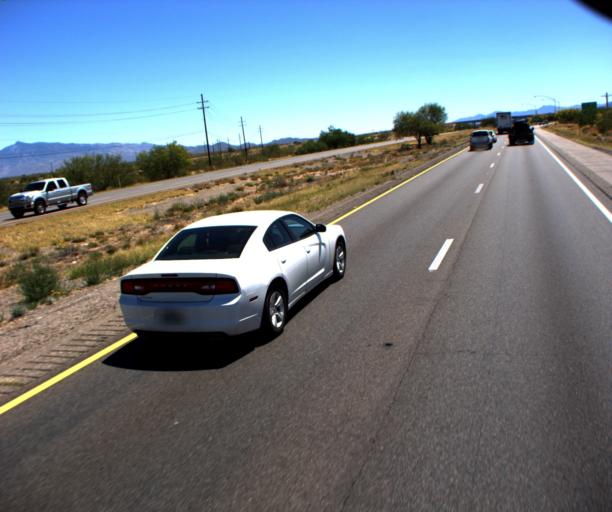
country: US
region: Arizona
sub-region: Pima County
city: Vail
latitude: 32.0846
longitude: -110.8106
